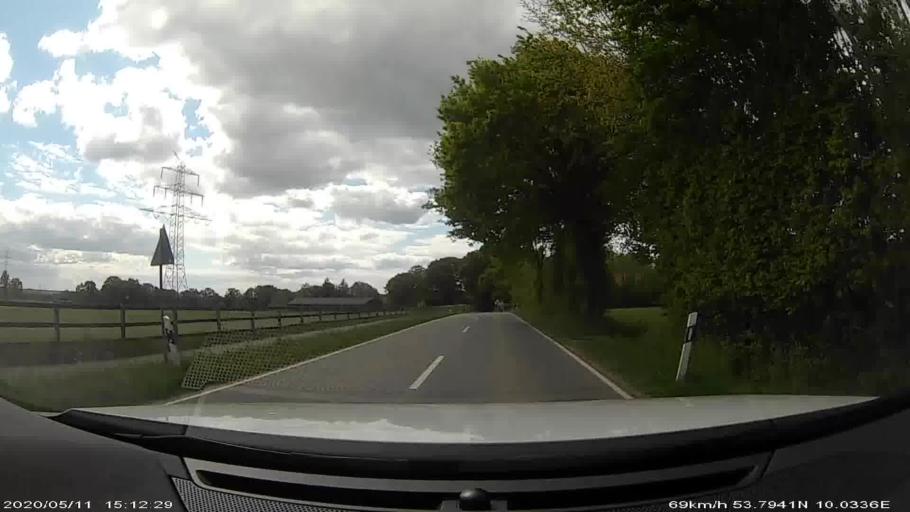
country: DE
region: Schleswig-Holstein
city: Kisdorf
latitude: 53.7887
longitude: 10.0124
